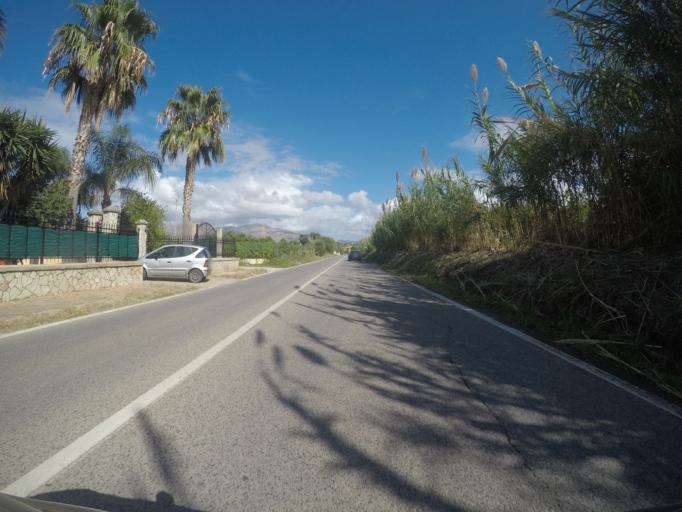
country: IT
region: Sicily
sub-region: Palermo
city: Trappeto
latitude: 38.0719
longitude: 13.0607
